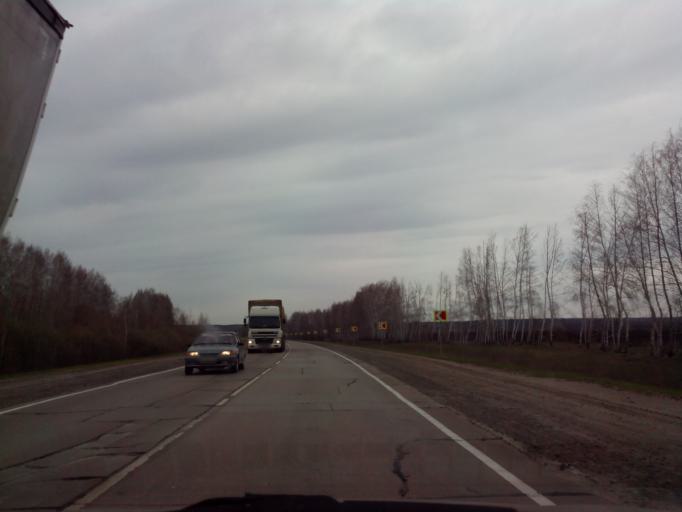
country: RU
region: Tambov
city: Znamenka
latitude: 52.5160
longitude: 41.3645
